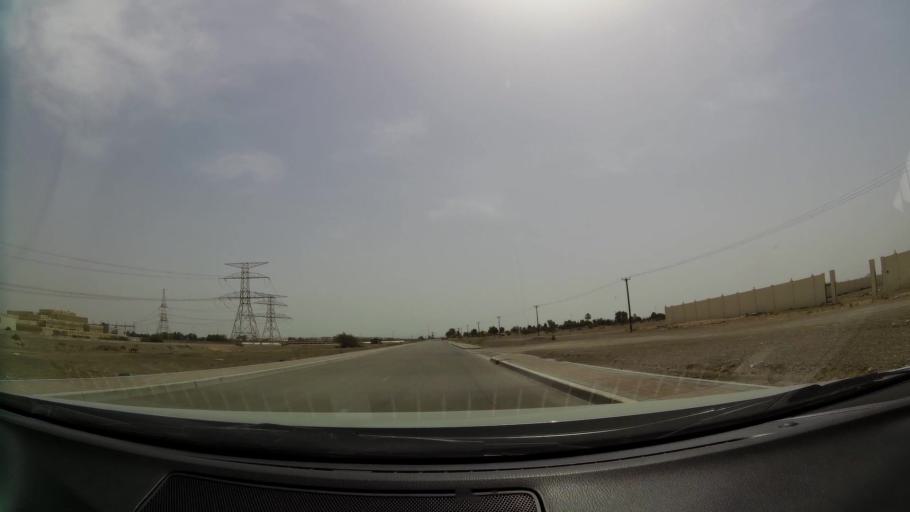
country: AE
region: Abu Dhabi
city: Al Ain
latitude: 24.1858
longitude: 55.6944
